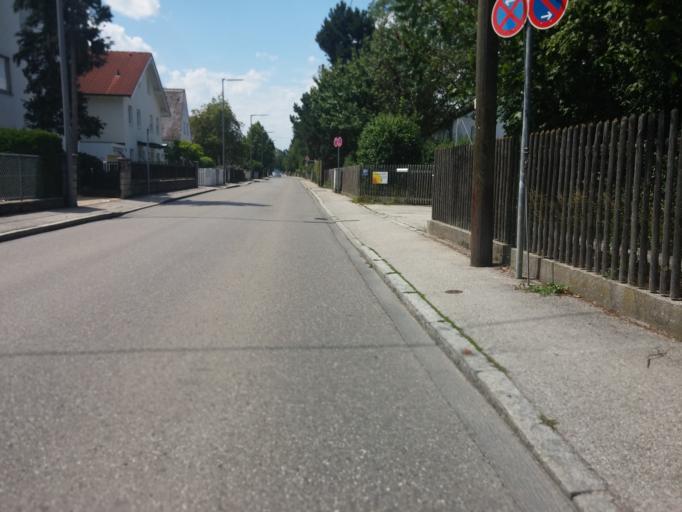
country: DE
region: Bavaria
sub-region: Upper Bavaria
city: Neubiberg
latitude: 48.1113
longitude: 11.6559
